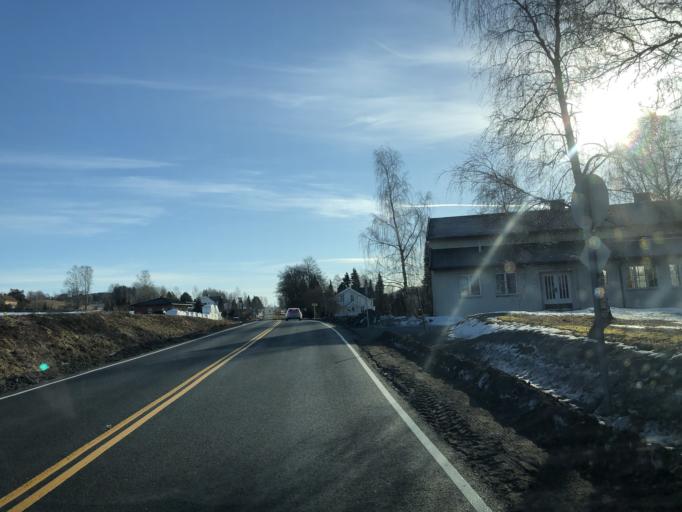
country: NO
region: Hedmark
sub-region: Ringsaker
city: Moelv
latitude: 60.9027
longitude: 10.7288
